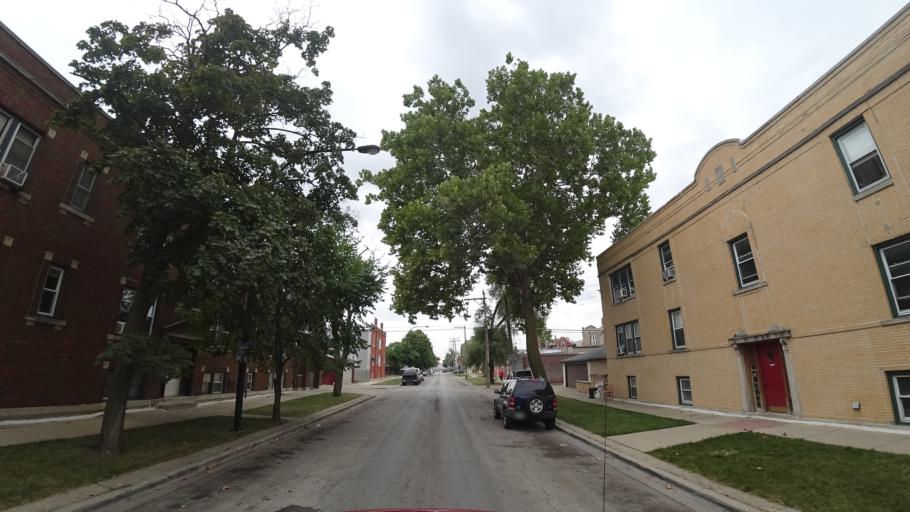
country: US
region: Illinois
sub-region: Cook County
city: Cicero
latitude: 41.8473
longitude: -87.7614
